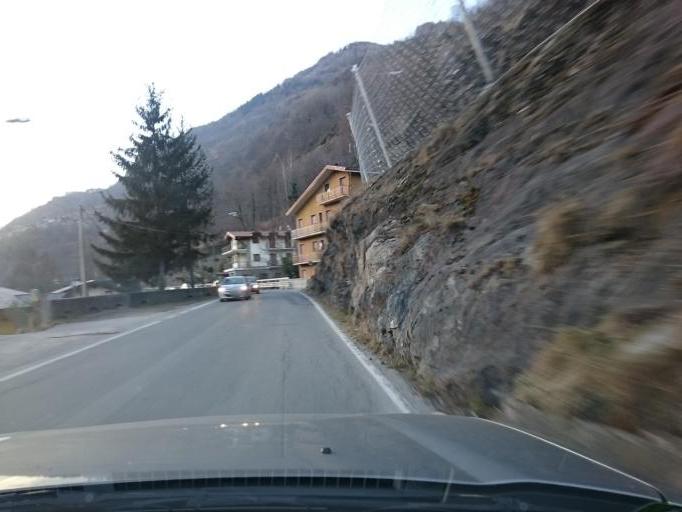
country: IT
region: Lombardy
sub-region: Provincia di Brescia
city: Corteno Golgi
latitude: 46.1747
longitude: 10.2732
